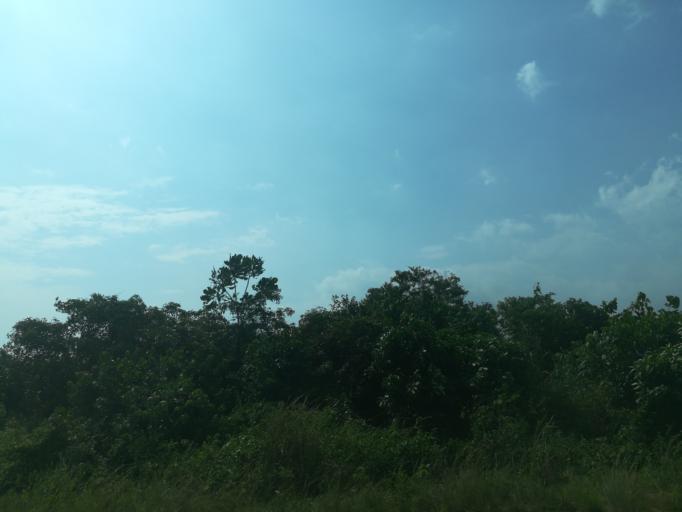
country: NG
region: Lagos
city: Ikorodu
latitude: 6.6344
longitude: 3.6695
